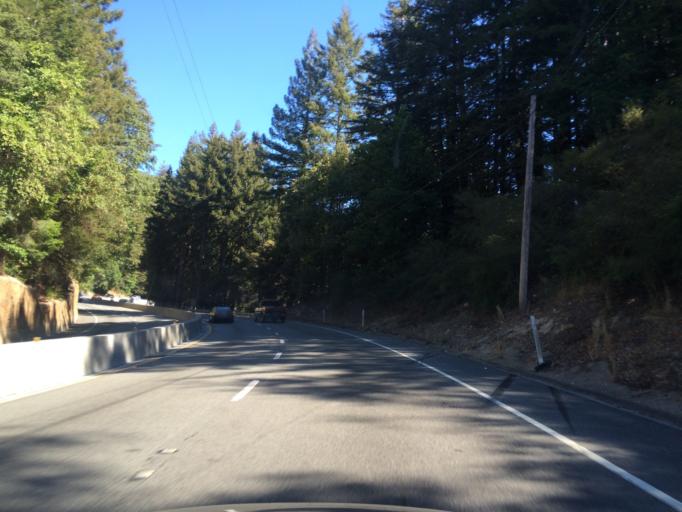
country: US
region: California
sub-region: Santa Clara County
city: Lexington Hills
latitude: 37.1142
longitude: -121.9744
